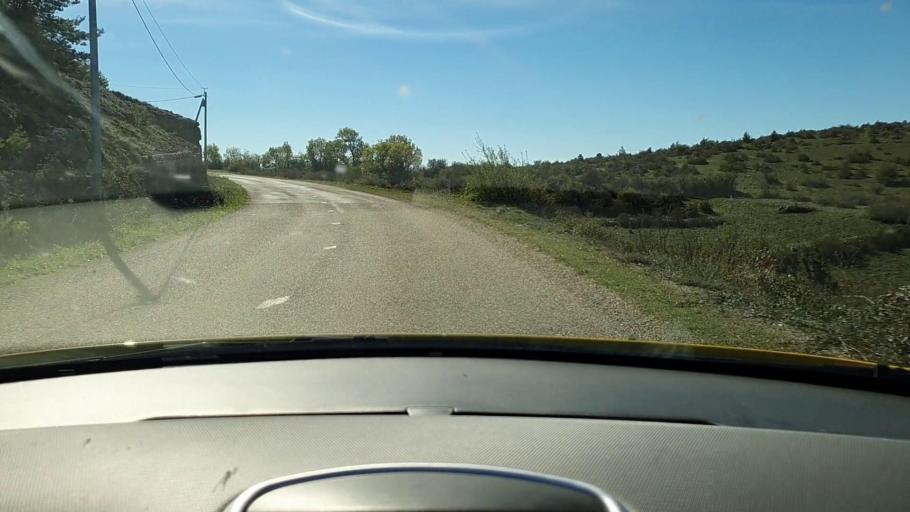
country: FR
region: Languedoc-Roussillon
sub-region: Departement du Gard
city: Aveze
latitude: 43.9607
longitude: 3.4078
